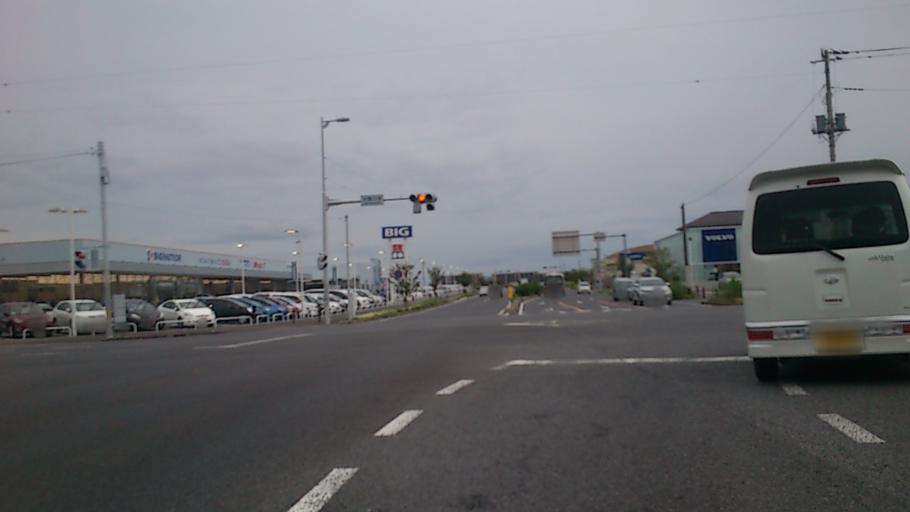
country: JP
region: Ibaraki
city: Naka
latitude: 36.1004
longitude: 140.0826
